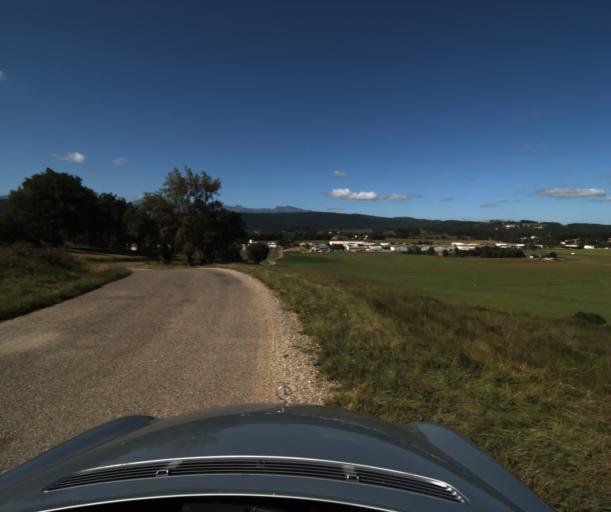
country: FR
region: Midi-Pyrenees
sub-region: Departement de l'Ariege
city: Lavelanet
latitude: 42.9875
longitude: 1.8803
